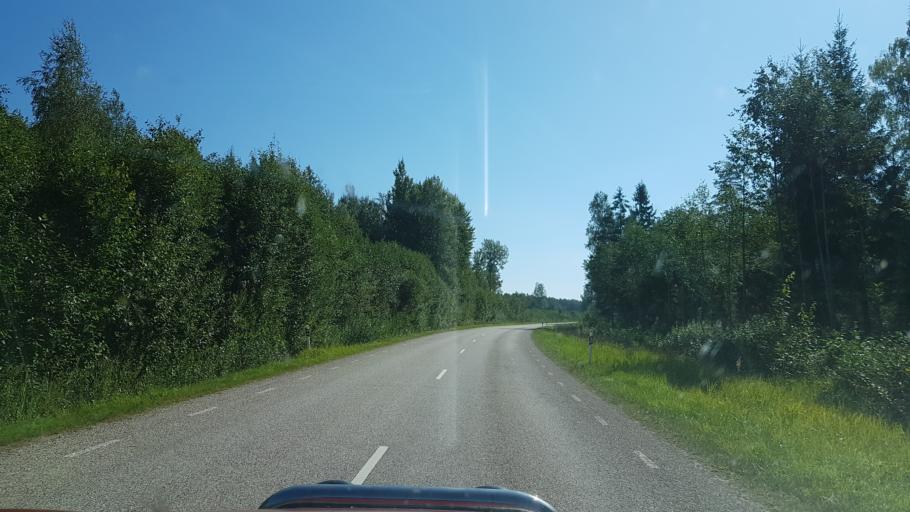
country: EE
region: Polvamaa
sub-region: Polva linn
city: Polva
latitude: 58.2629
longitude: 27.1734
